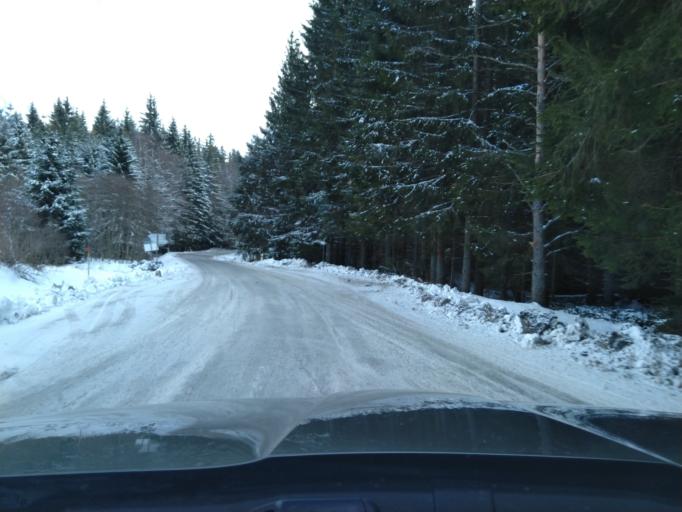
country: CZ
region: Jihocesky
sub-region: Okres Prachatice
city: Zdikov
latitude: 49.0480
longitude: 13.6646
